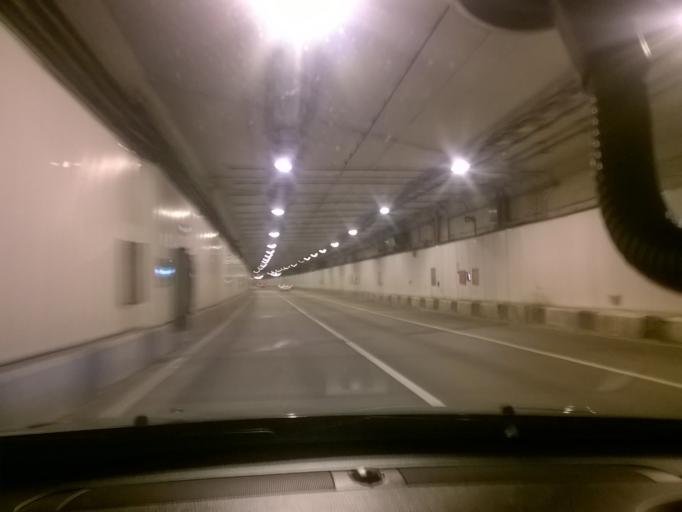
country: RU
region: Moskovskaya
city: Koptevo
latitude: 55.8152
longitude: 37.5190
